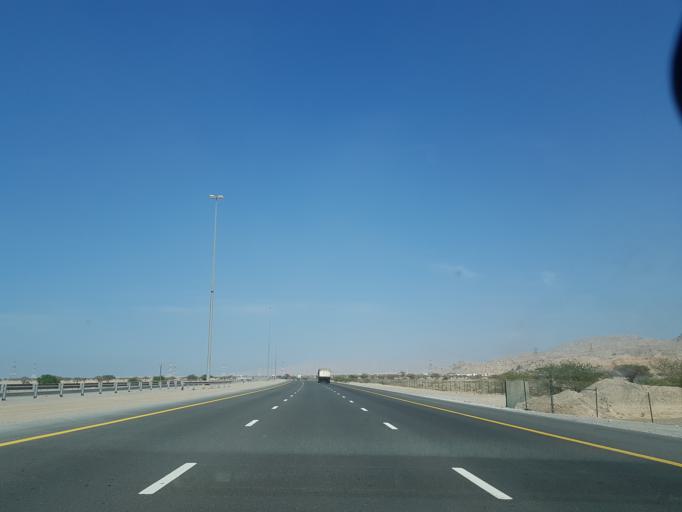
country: AE
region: Ra's al Khaymah
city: Ras al-Khaimah
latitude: 25.7318
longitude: 56.0145
